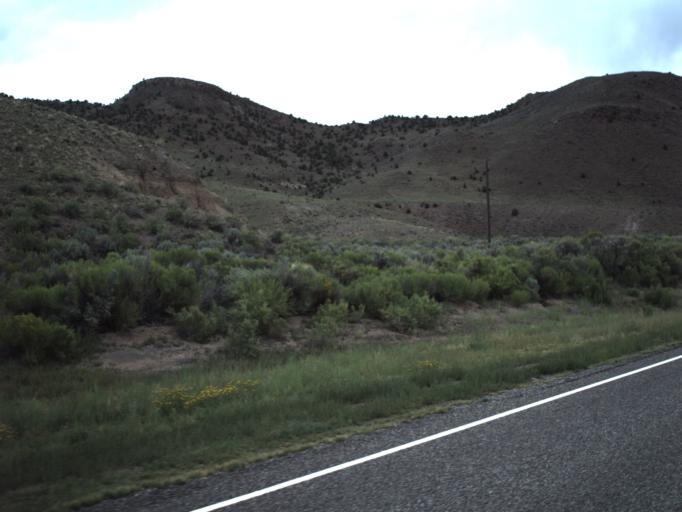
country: US
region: Utah
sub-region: Piute County
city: Junction
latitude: 38.1689
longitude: -112.0476
